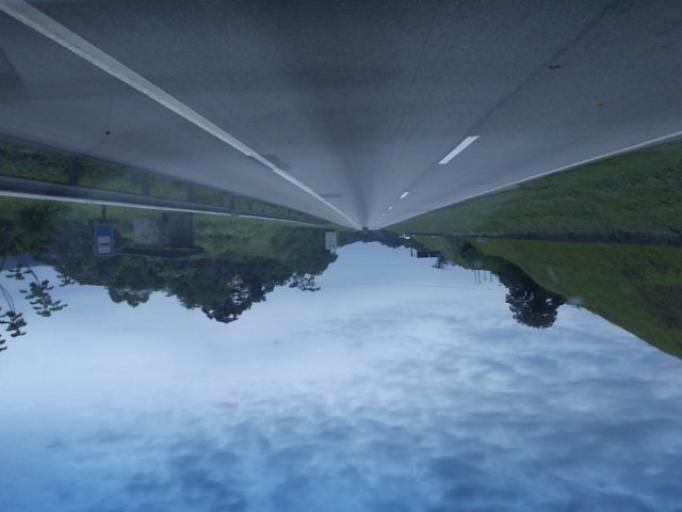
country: BR
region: Sao Paulo
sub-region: Miracatu
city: Miracatu
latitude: -24.1723
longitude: -47.3416
